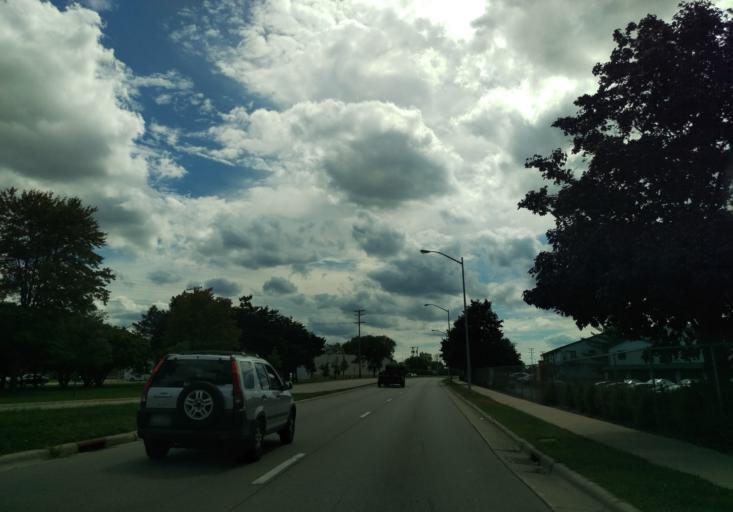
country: US
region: Wisconsin
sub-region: Dane County
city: Maple Bluff
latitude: 43.1273
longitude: -89.3560
